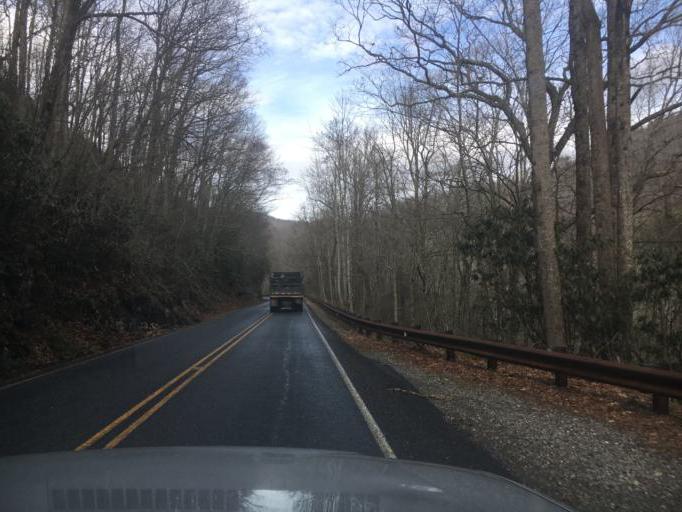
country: US
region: North Carolina
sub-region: Haywood County
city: Canton
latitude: 35.3805
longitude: -82.8106
